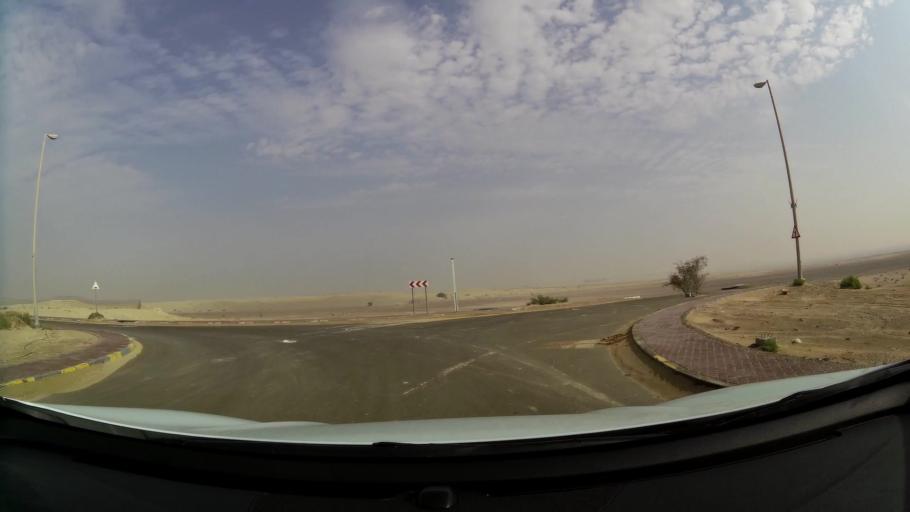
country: AE
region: Abu Dhabi
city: Abu Dhabi
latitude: 24.2568
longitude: 54.7220
